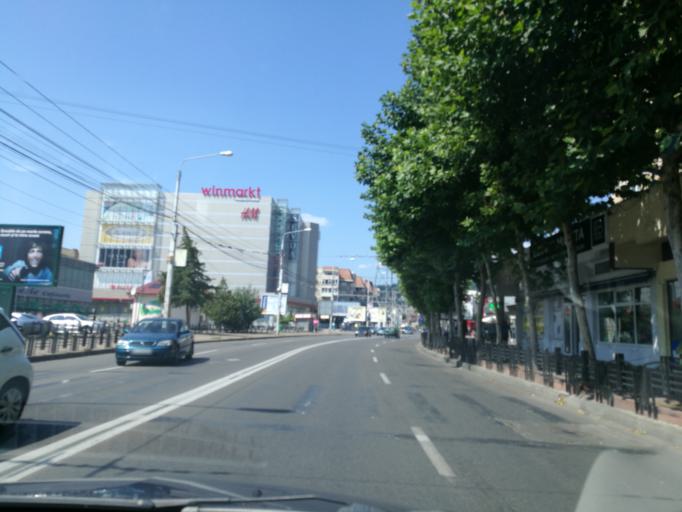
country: RO
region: Neamt
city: Piatra Neamt
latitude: 46.9301
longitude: 26.3643
